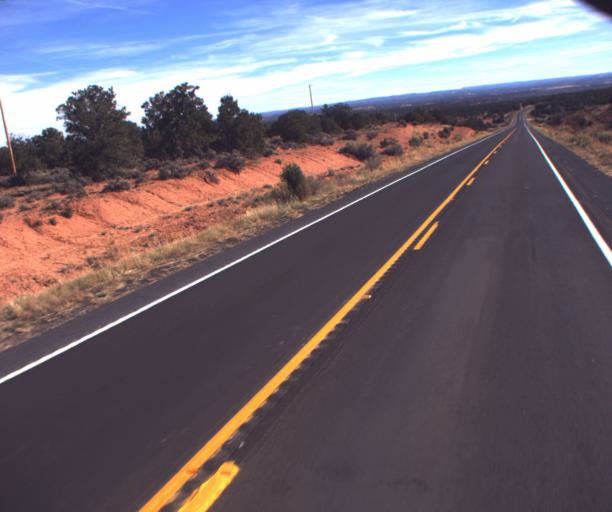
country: US
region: Arizona
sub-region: Coconino County
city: Kaibito
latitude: 36.5839
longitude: -110.8299
